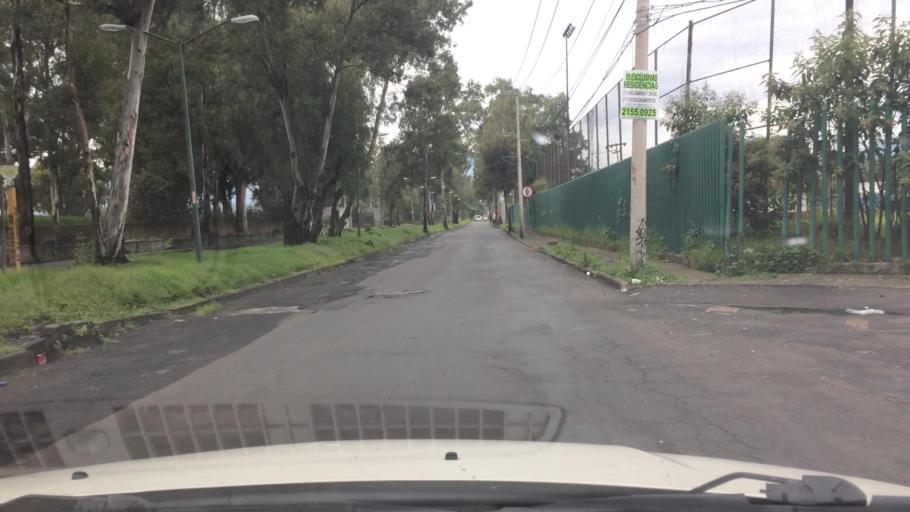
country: MX
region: Mexico City
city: Iztapalapa
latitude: 19.3139
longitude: -99.0999
